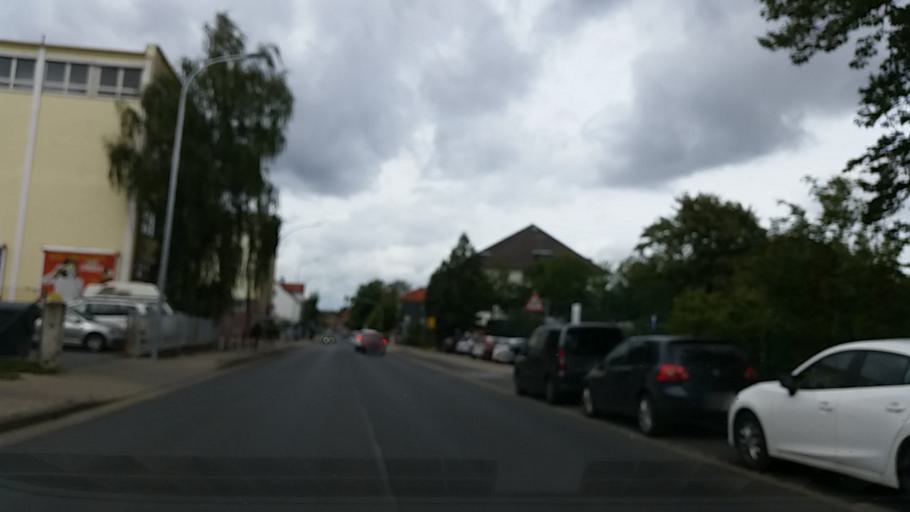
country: DE
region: Lower Saxony
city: Wolfenbuettel
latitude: 52.1578
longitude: 10.5504
